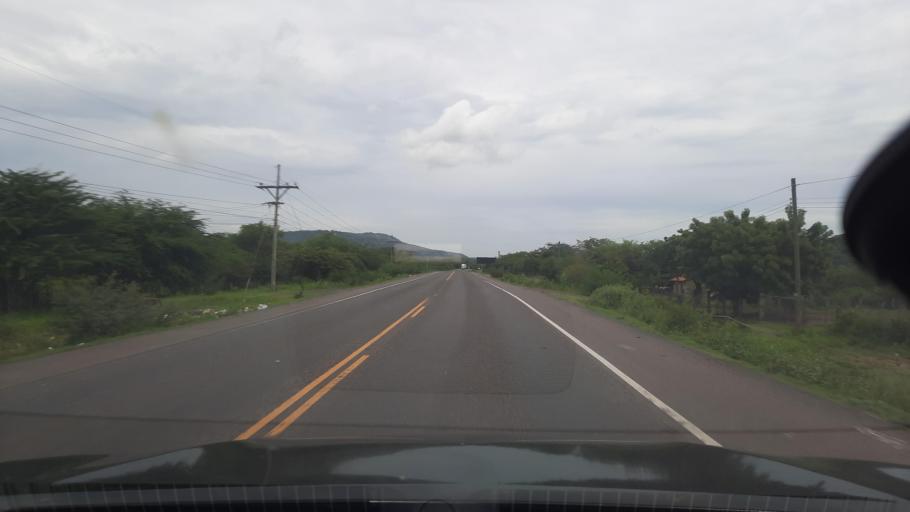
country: HN
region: Valle
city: Jicaro Galan
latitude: 13.5190
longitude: -87.4396
